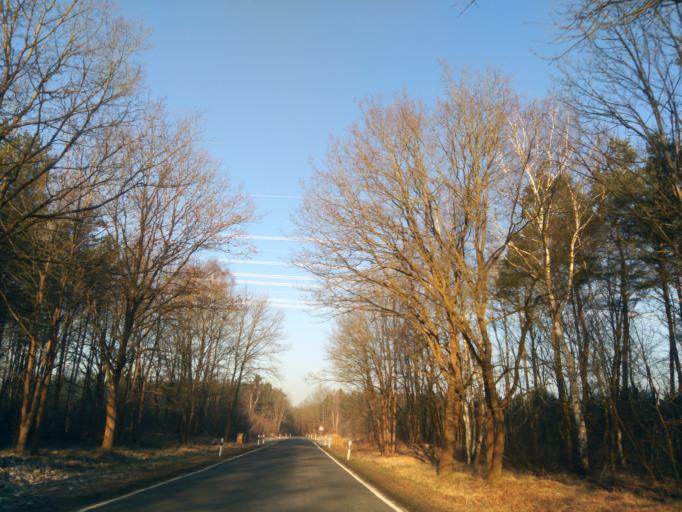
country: DE
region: Brandenburg
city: Falkensee
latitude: 52.6287
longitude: 13.0808
